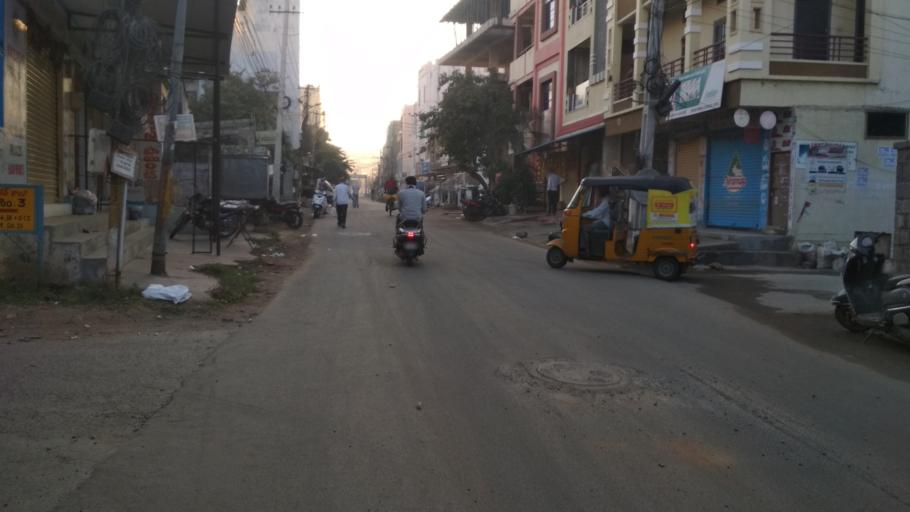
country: IN
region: Telangana
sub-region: Rangareddi
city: Lal Bahadur Nagar
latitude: 17.3365
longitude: 78.5483
